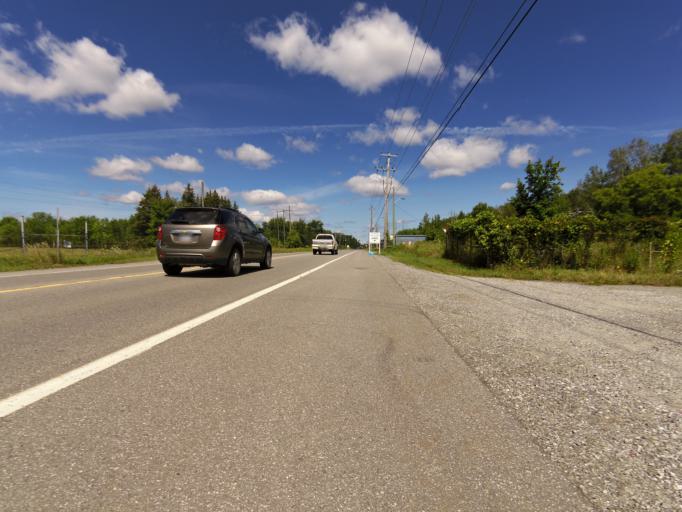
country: CA
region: Ontario
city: Ottawa
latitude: 45.3331
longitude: -75.6589
